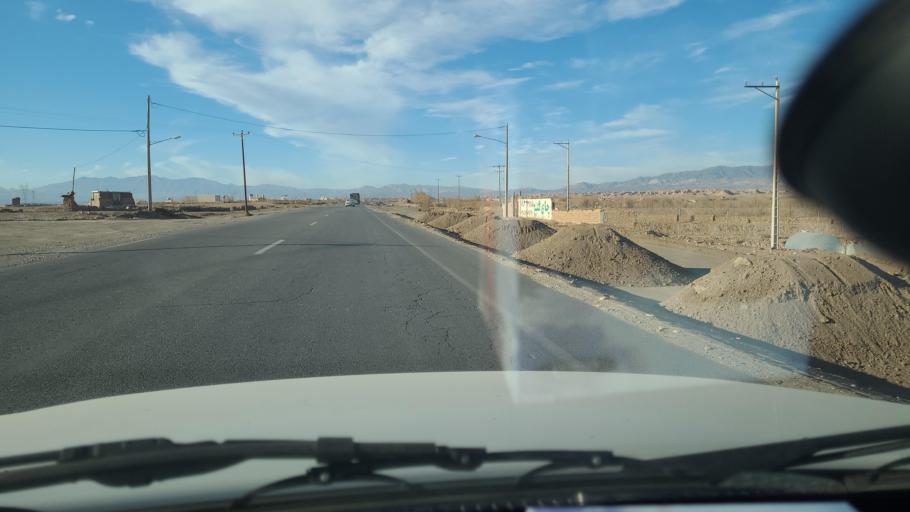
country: IR
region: Razavi Khorasan
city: Sabzevar
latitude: 36.2349
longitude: 57.6450
